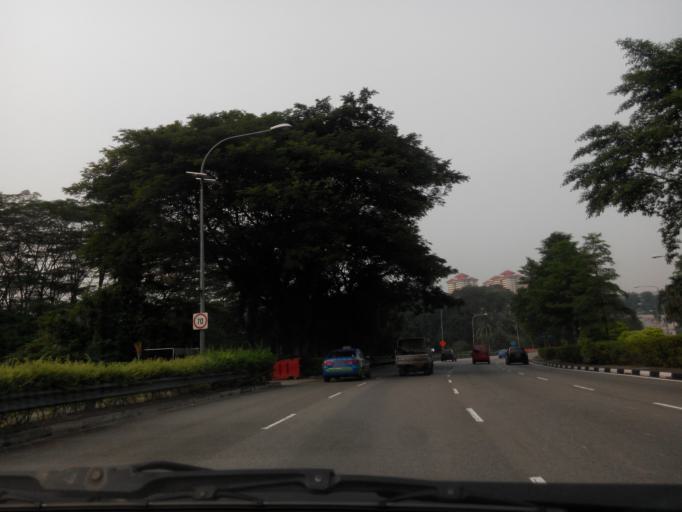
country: SG
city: Singapore
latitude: 1.2924
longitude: 103.7984
